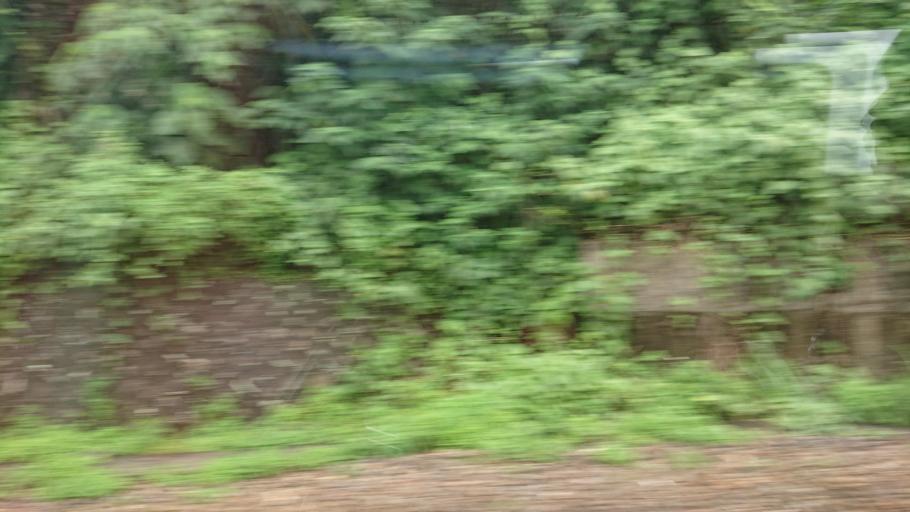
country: TW
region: Taiwan
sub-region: Yilan
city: Yilan
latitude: 24.9083
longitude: 121.8734
